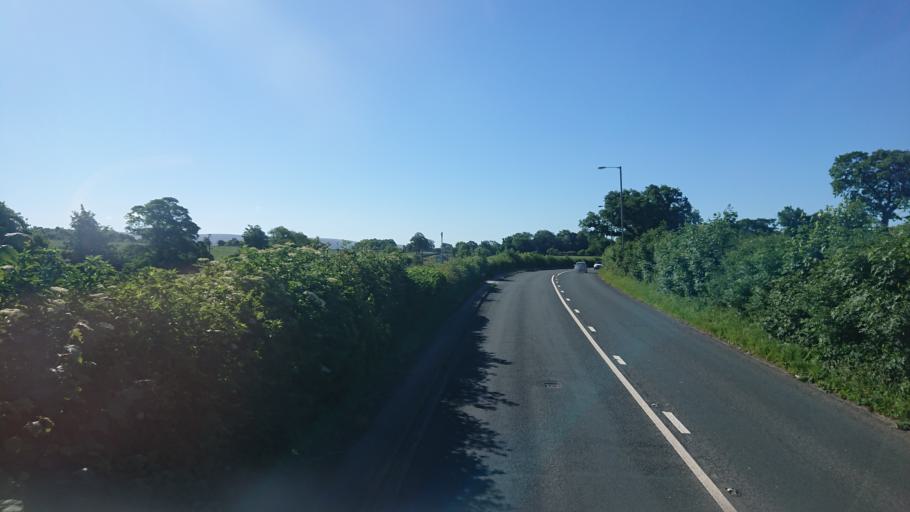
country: GB
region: England
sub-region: Lancashire
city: Galgate
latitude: 53.9852
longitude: -2.7877
